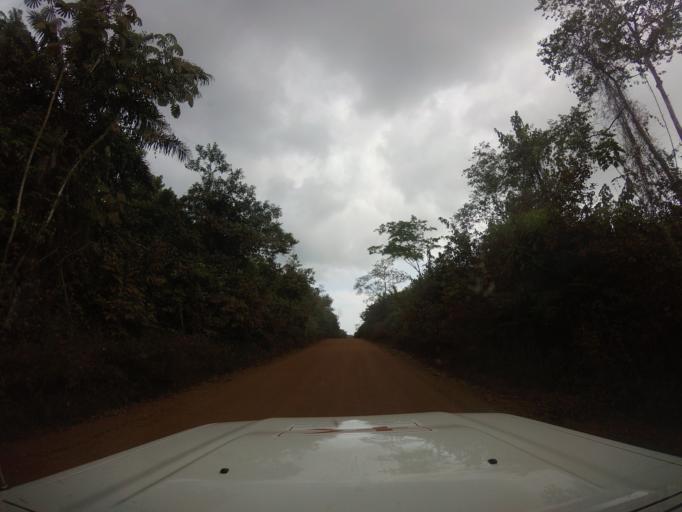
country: LR
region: Grand Cape Mount
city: Robertsport
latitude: 6.7243
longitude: -11.3366
